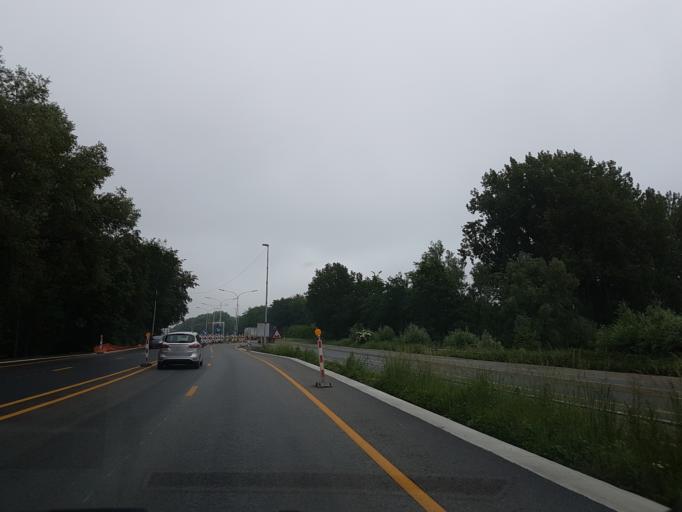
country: BE
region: Flanders
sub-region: Provincie Oost-Vlaanderen
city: Aalst
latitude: 50.9327
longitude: 4.0161
